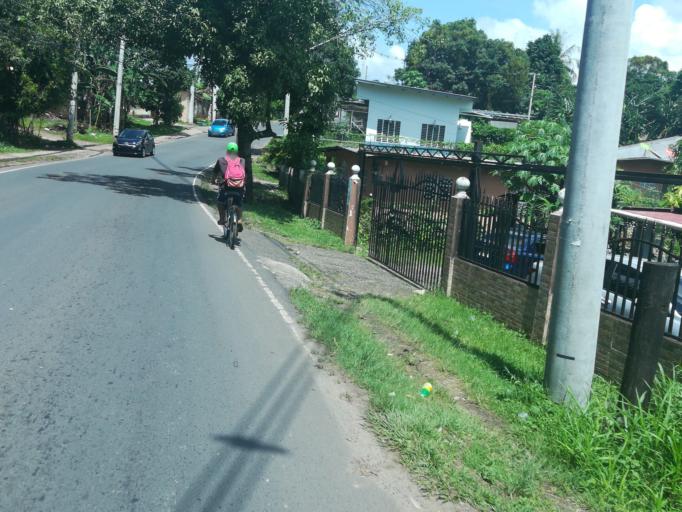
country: PA
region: Panama
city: Tocumen
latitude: 9.0886
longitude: -79.4063
